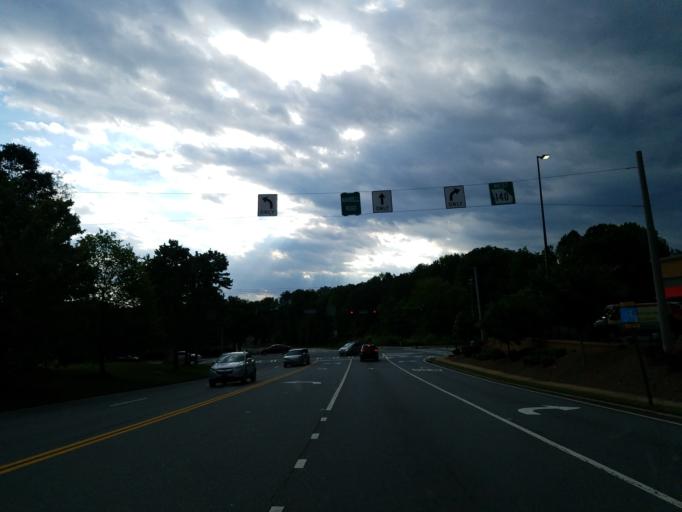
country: US
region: Georgia
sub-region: Fulton County
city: Roswell
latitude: 34.0431
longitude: -84.3428
